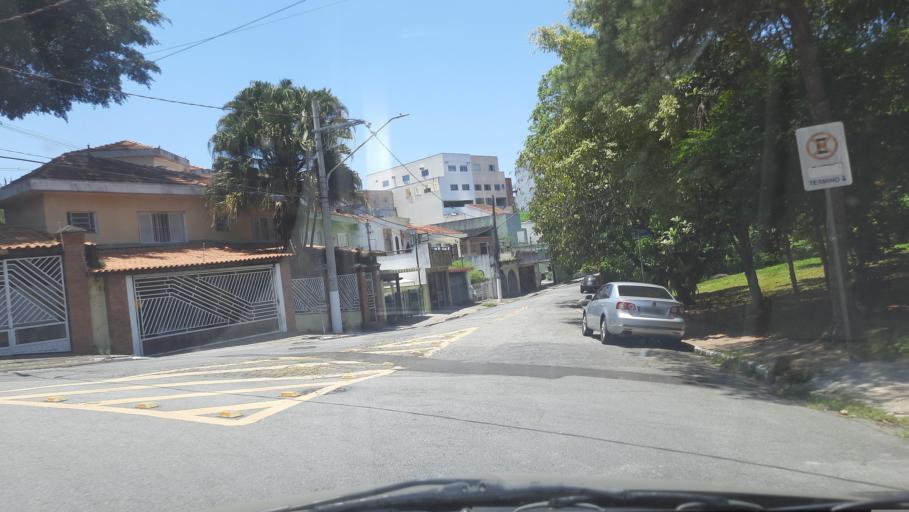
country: BR
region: Sao Paulo
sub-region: Osasco
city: Osasco
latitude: -23.4914
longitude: -46.7382
